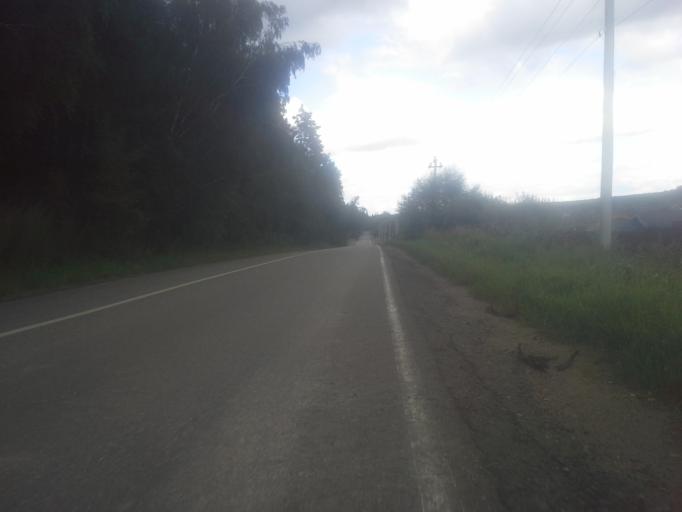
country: RU
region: Moskovskaya
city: Karinskoye
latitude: 55.6614
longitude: 36.6386
